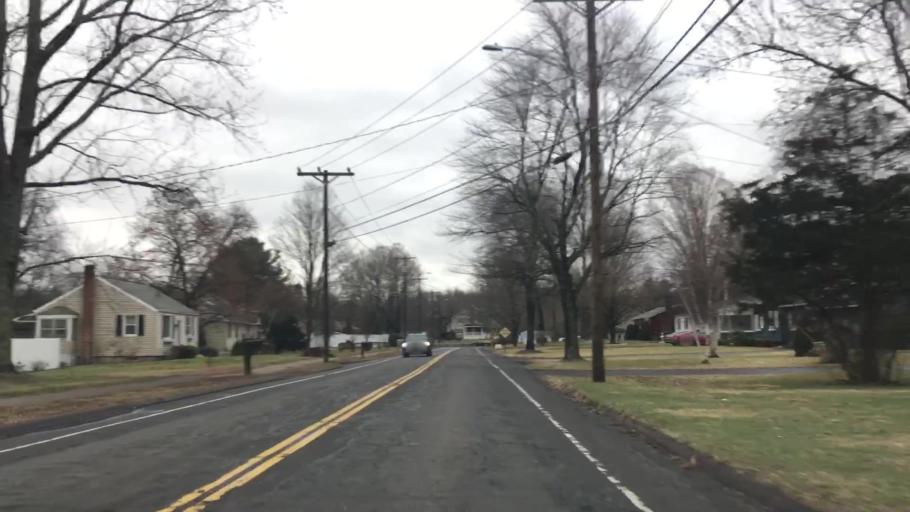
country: US
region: Connecticut
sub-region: Tolland County
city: Rockville
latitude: 41.8529
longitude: -72.4925
